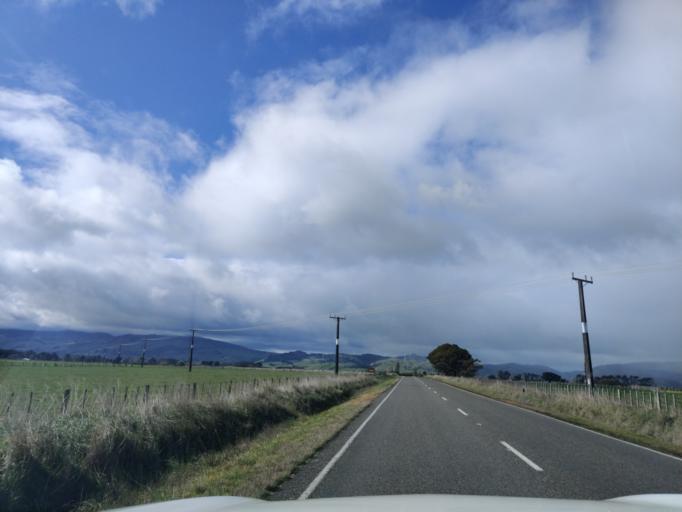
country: NZ
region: Manawatu-Wanganui
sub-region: Palmerston North City
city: Palmerston North
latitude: -40.2902
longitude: 175.7172
